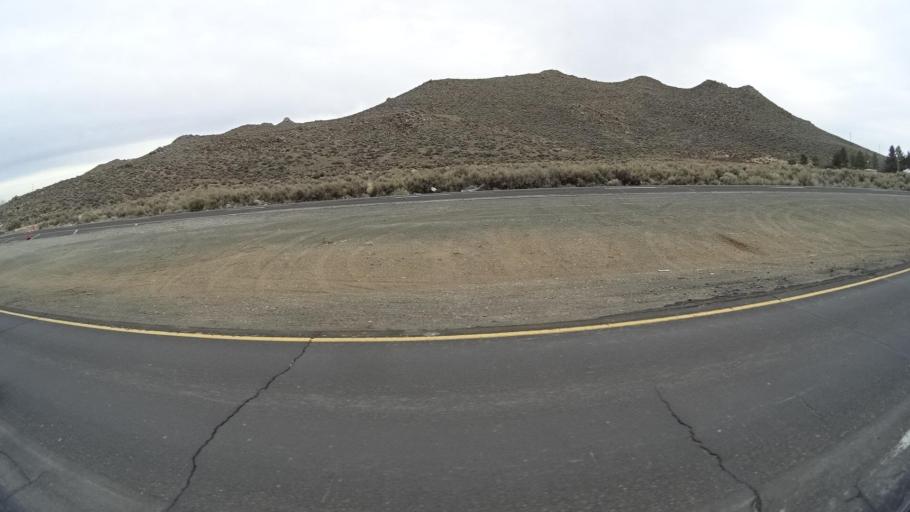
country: US
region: Nevada
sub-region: Washoe County
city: Lemmon Valley
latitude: 39.6252
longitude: -119.8478
